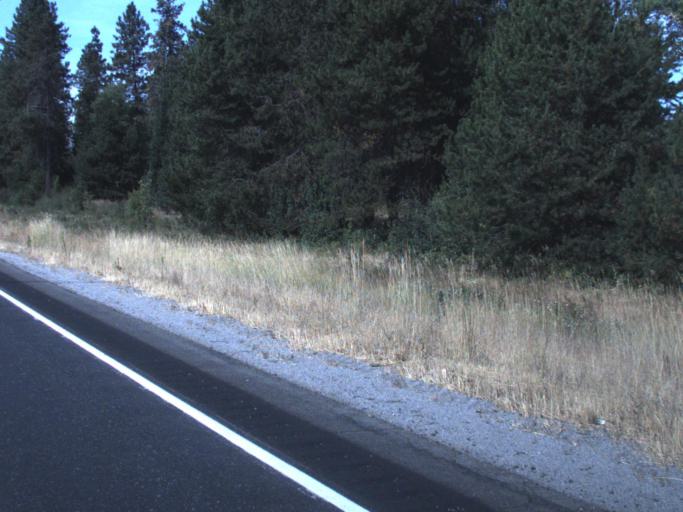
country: US
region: Washington
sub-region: Spokane County
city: Deer Park
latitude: 47.9936
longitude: -117.5530
